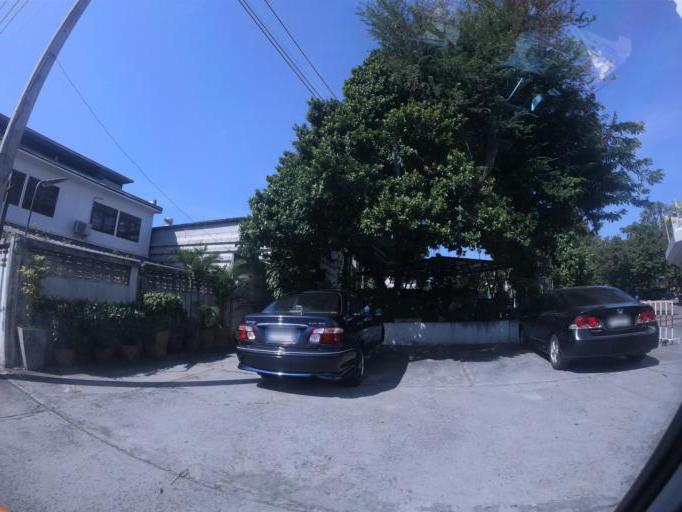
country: TH
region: Maha Sarakham
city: Chiang Yuen
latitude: 16.3792
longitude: 102.9694
